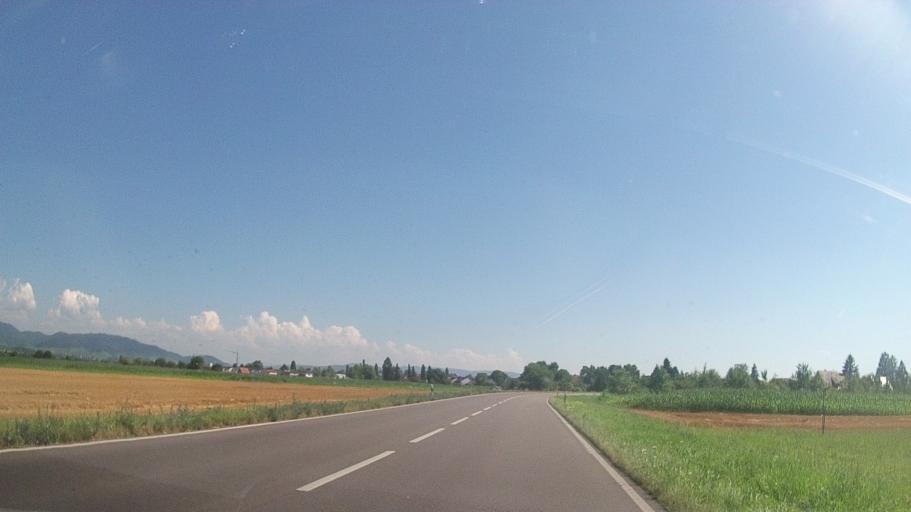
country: DE
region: Baden-Wuerttemberg
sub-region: Freiburg Region
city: Willstatt
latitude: 48.5158
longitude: 7.9255
